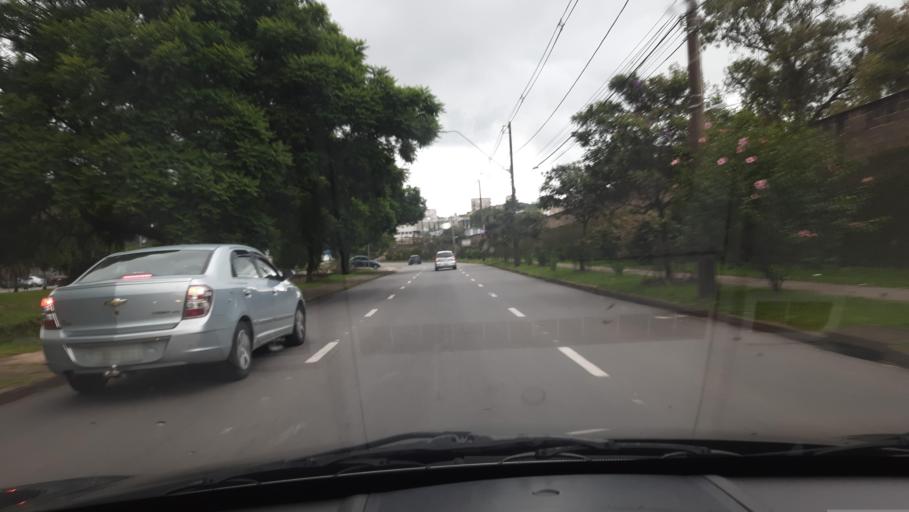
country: BR
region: Minas Gerais
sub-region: Pocos De Caldas
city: Pocos de Caldas
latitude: -21.7826
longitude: -46.5977
